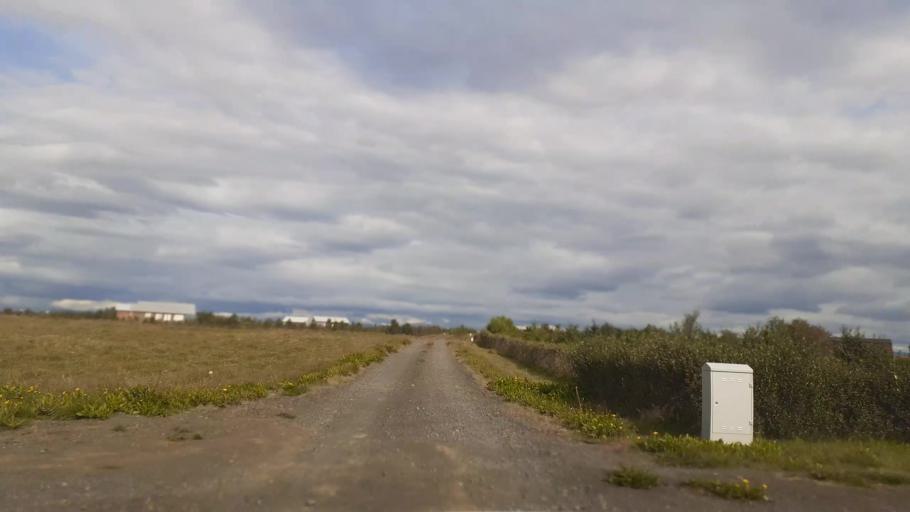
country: IS
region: South
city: Vestmannaeyjar
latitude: 63.7711
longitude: -20.2976
